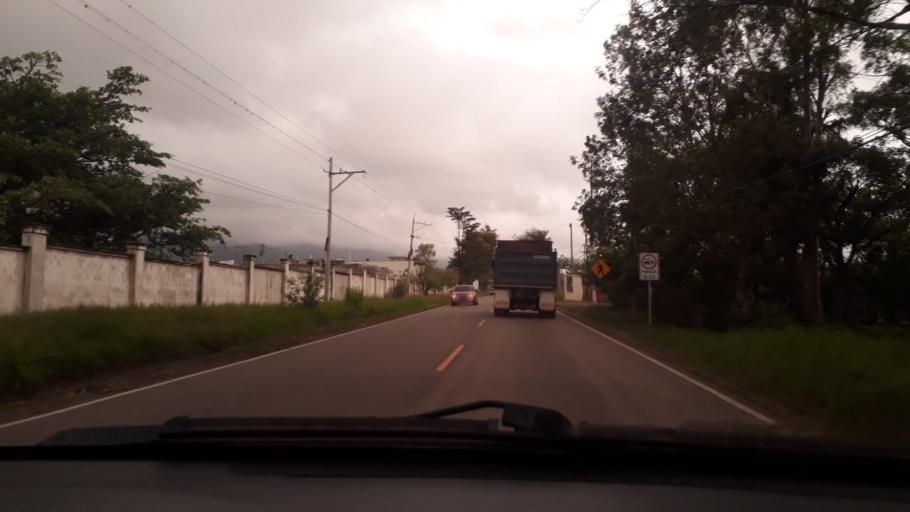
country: GT
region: Chiquimula
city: Esquipulas
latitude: 14.5618
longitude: -89.3302
